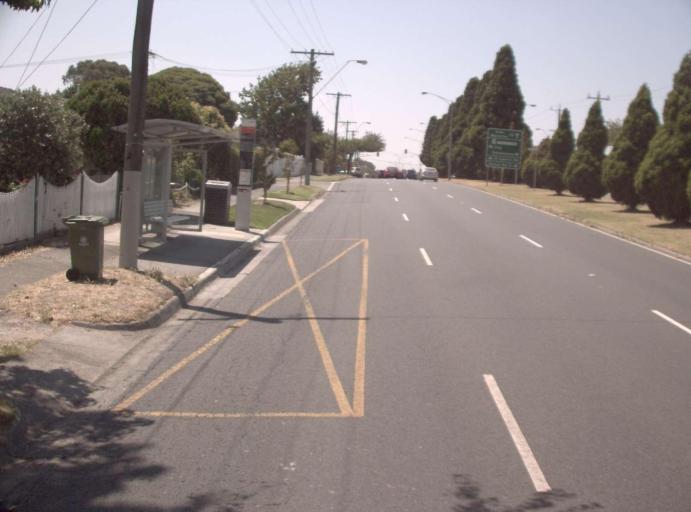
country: AU
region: Victoria
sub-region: Greater Dandenong
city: Springvale
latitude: -37.9373
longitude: 145.1548
